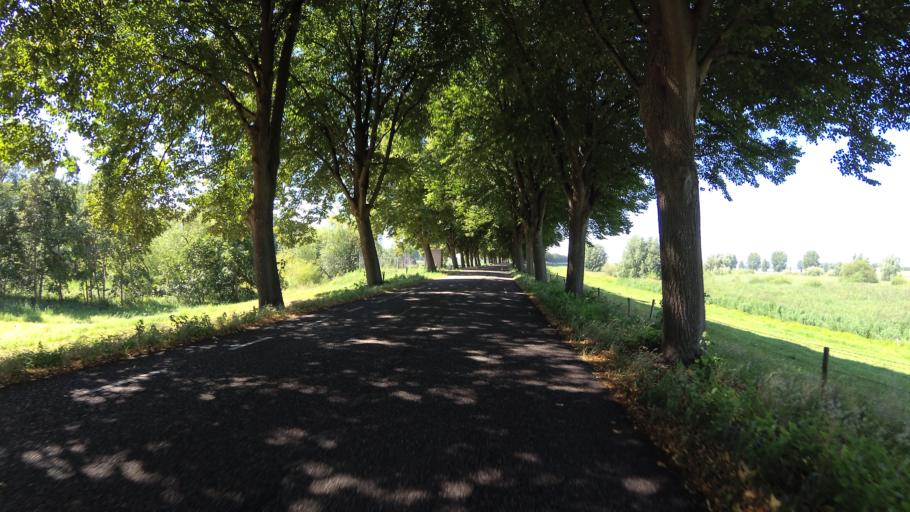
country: NL
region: North Brabant
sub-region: Gemeente Waalwijk
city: Waalwijk
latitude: 51.7133
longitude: 5.0716
